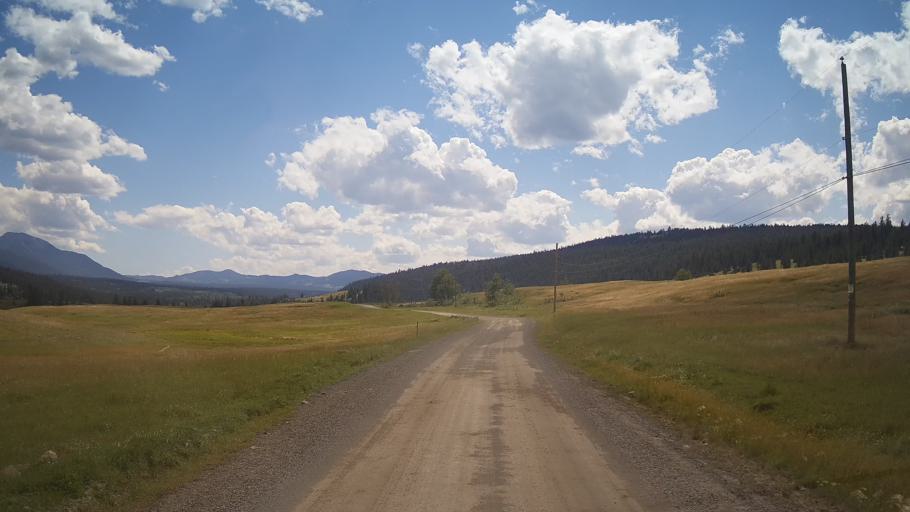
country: CA
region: British Columbia
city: Lillooet
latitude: 51.3123
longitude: -121.9840
